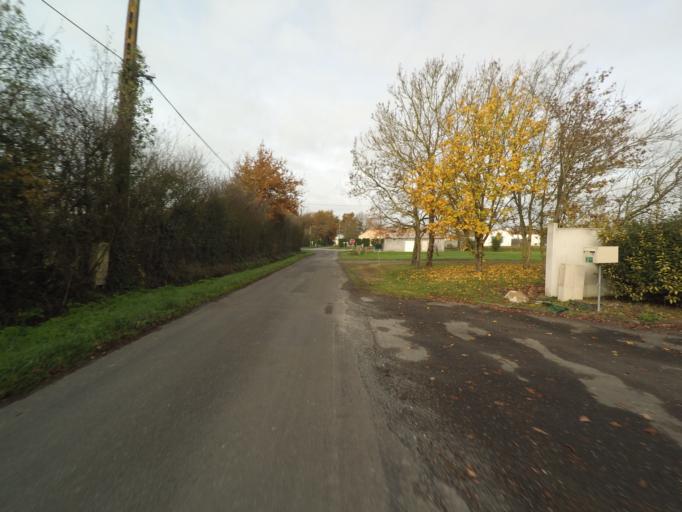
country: FR
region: Pays de la Loire
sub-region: Departement de la Loire-Atlantique
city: La Planche
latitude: 47.0237
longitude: -1.4080
